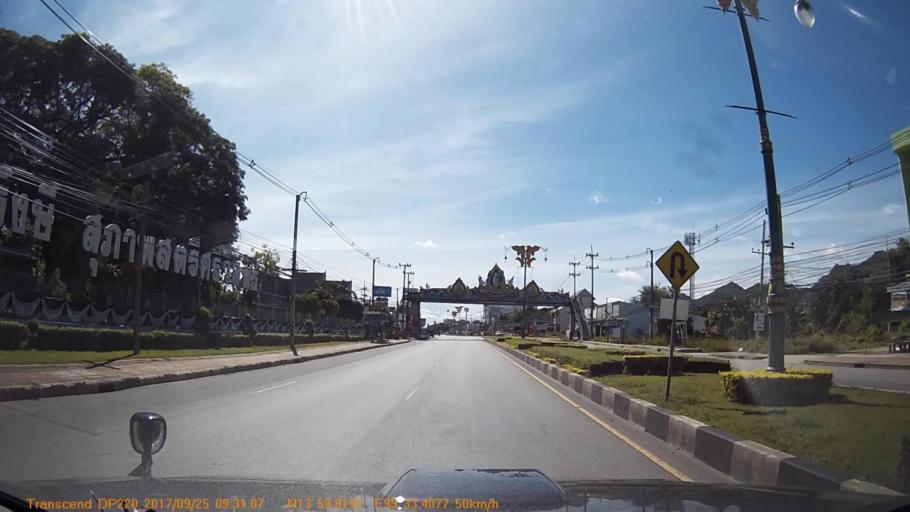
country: TH
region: Kanchanaburi
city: Kanchanaburi
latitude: 13.9968
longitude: 99.5570
